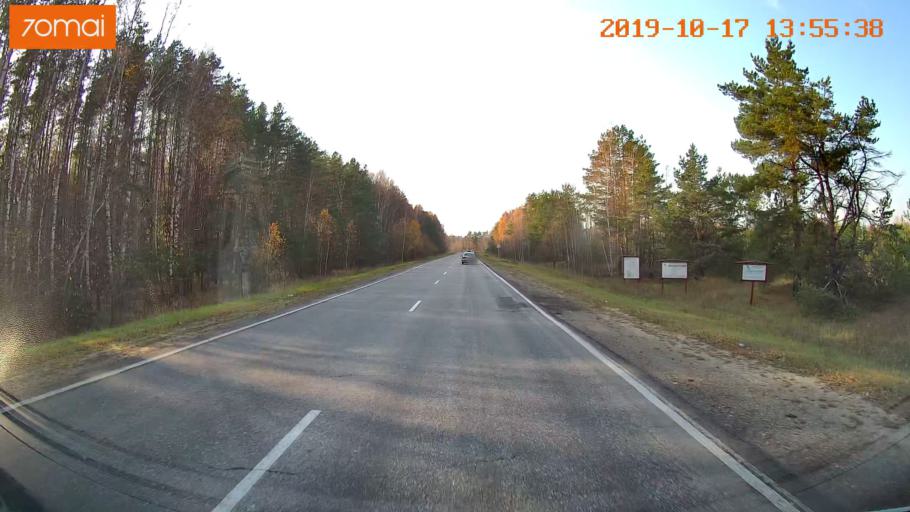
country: RU
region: Rjazan
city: Spas-Klepiki
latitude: 55.1525
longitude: 40.2840
